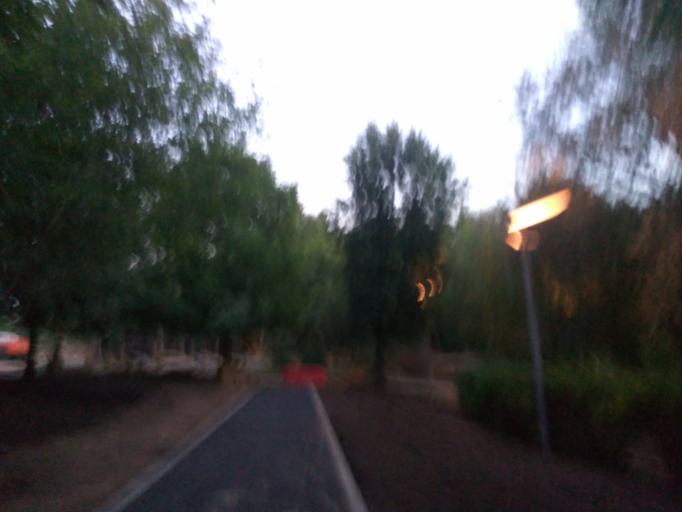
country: RU
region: Moskovskaya
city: Levoberezhnaya
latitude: 55.8774
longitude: 37.4676
